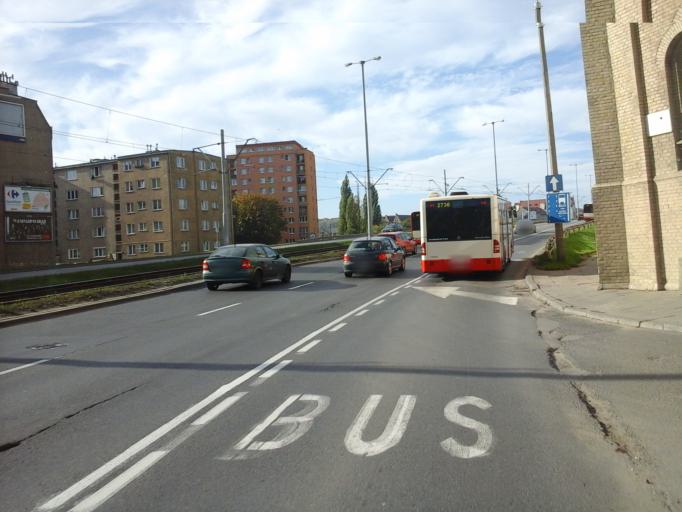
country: PL
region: Pomeranian Voivodeship
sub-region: Gdansk
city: Gdansk
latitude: 54.3447
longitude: 18.6633
